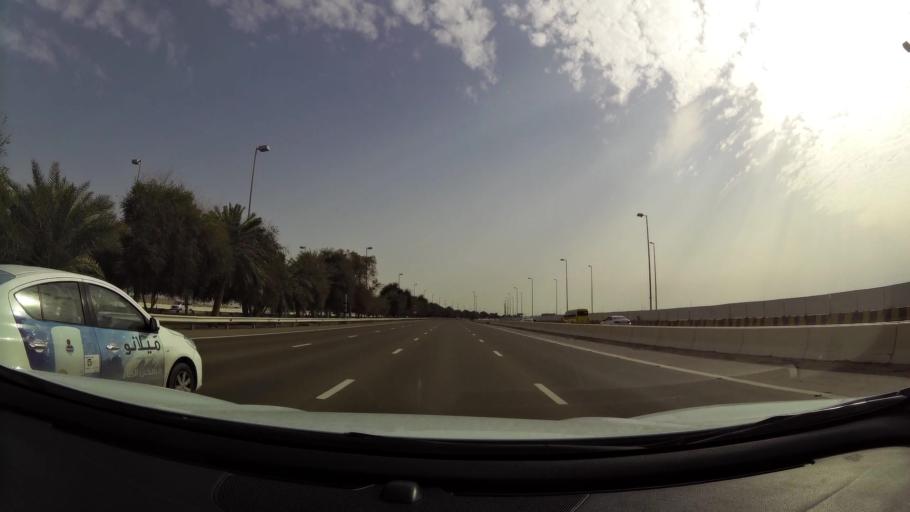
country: AE
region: Abu Dhabi
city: Abu Dhabi
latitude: 24.4231
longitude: 54.6773
